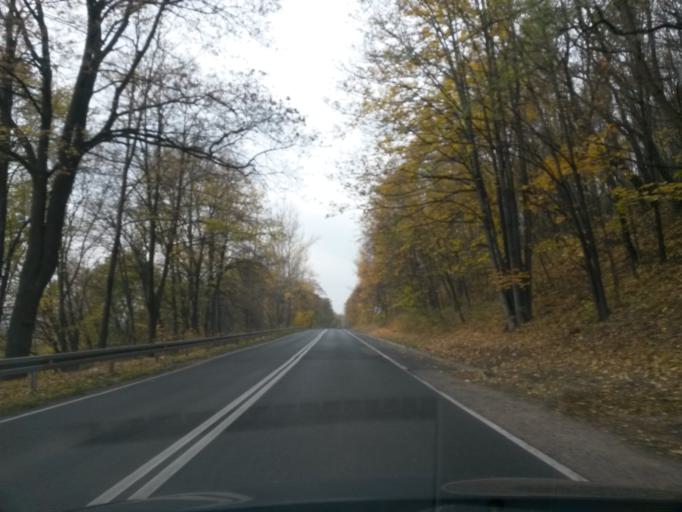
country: PL
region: Lower Silesian Voivodeship
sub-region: Powiat klodzki
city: Klodzko
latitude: 50.3823
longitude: 16.6683
